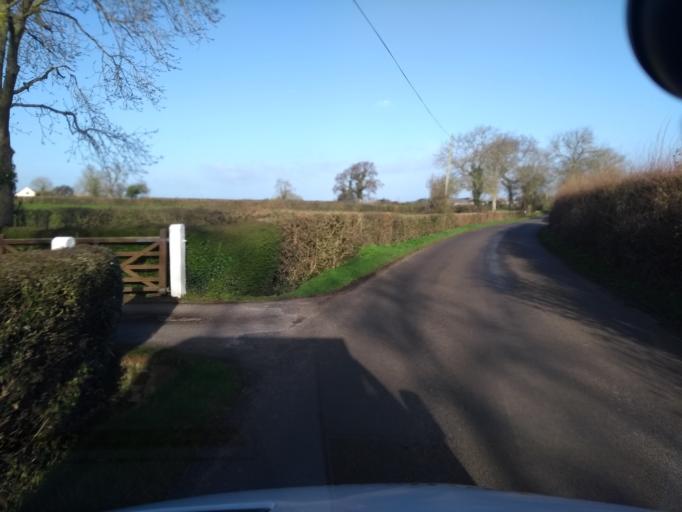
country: GB
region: England
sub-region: Somerset
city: Westonzoyland
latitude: 51.1444
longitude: -2.8626
